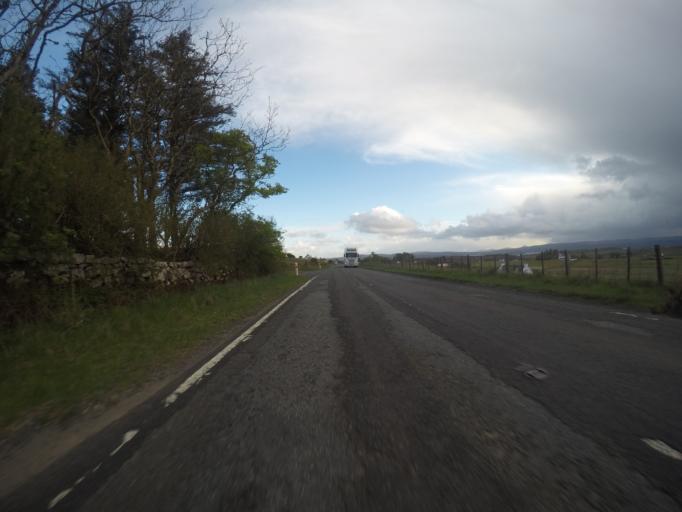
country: GB
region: Scotland
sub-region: Highland
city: Portree
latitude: 57.5686
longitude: -6.3647
